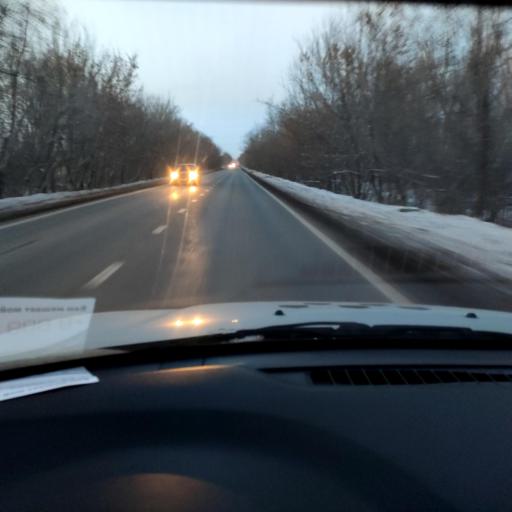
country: RU
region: Samara
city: Tol'yatti
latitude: 53.5477
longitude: 49.3936
